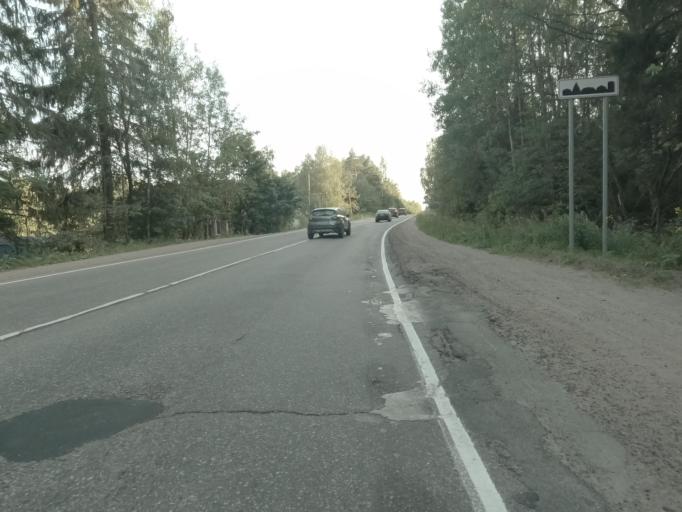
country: RU
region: Leningrad
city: Vyborg
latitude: 60.7432
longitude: 28.7679
